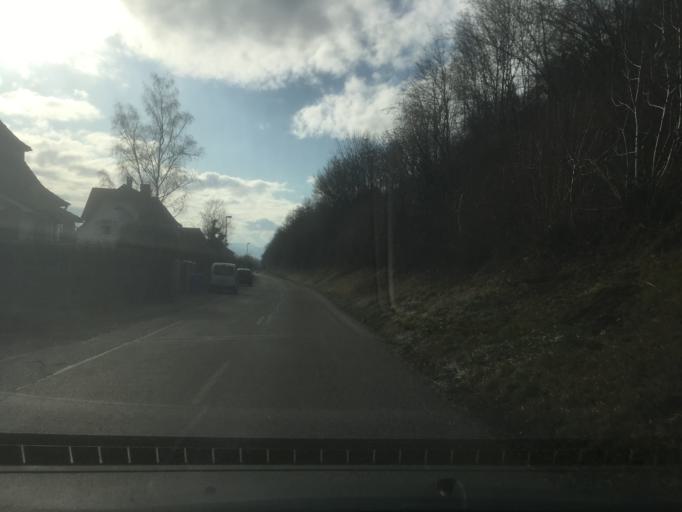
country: CH
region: Aargau
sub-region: Bezirk Zurzach
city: Koblenz
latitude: 47.6182
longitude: 8.2393
